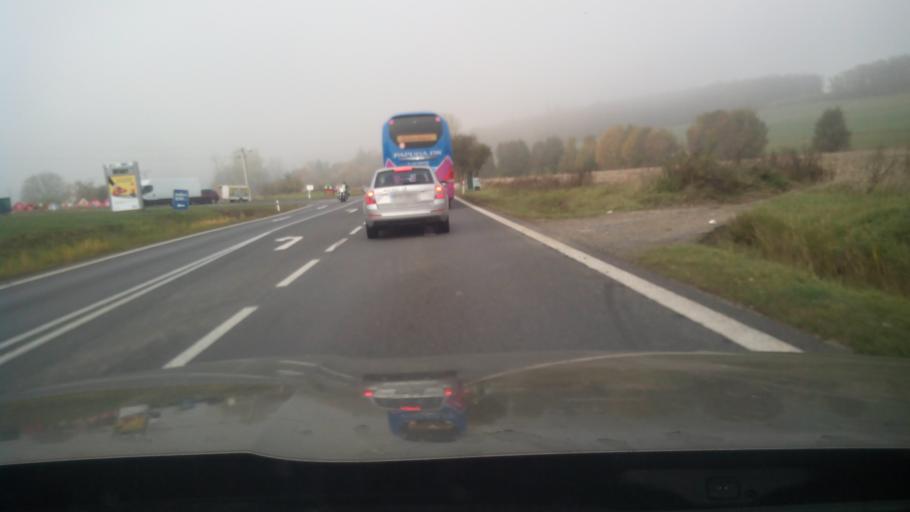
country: CZ
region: Central Bohemia
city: Milin
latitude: 49.5785
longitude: 14.0750
